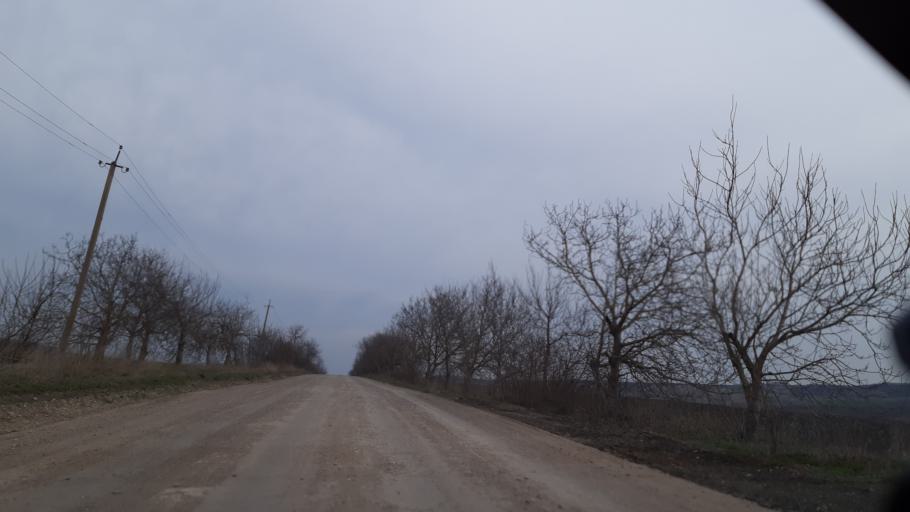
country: MD
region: Soldanesti
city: Soldanesti
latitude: 47.7015
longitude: 28.7212
